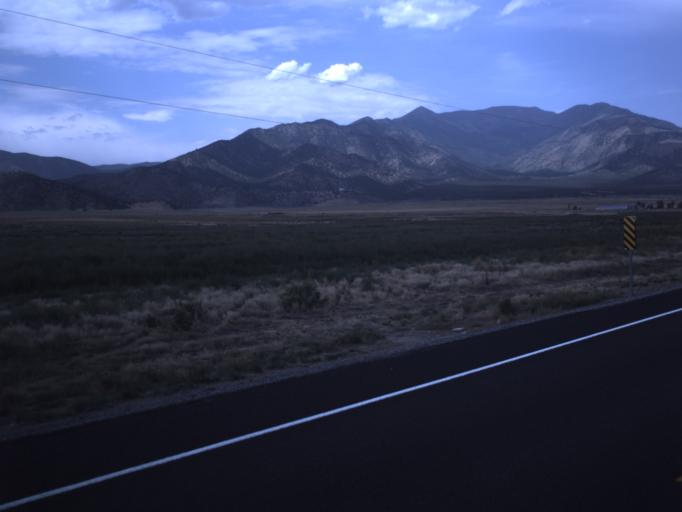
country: US
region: Utah
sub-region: Utah County
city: Eagle Mountain
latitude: 40.2735
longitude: -112.0940
